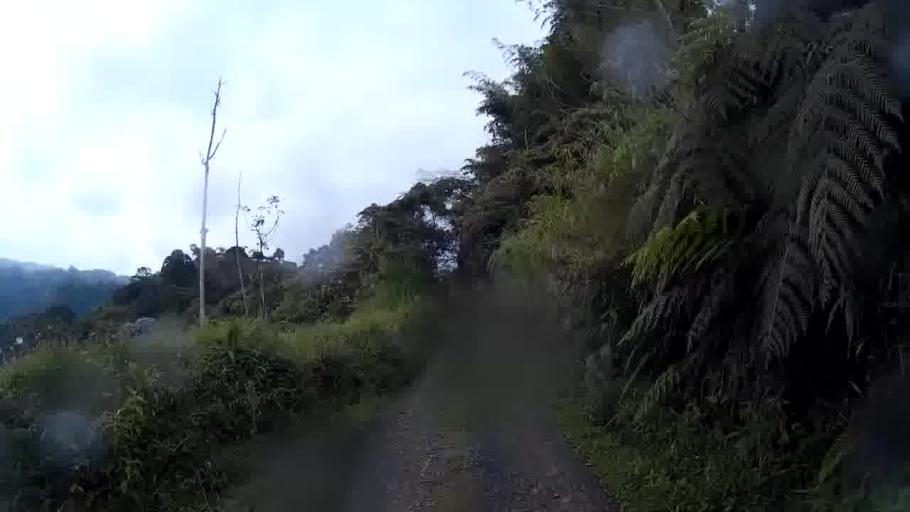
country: CO
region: Quindio
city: Filandia
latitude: 4.7061
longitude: -75.6774
